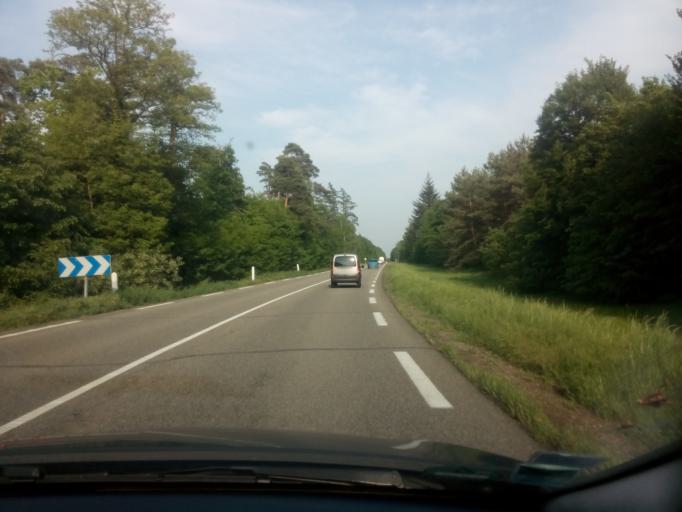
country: FR
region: Alsace
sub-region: Departement du Bas-Rhin
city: Soufflenheim
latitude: 48.8366
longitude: 7.9145
